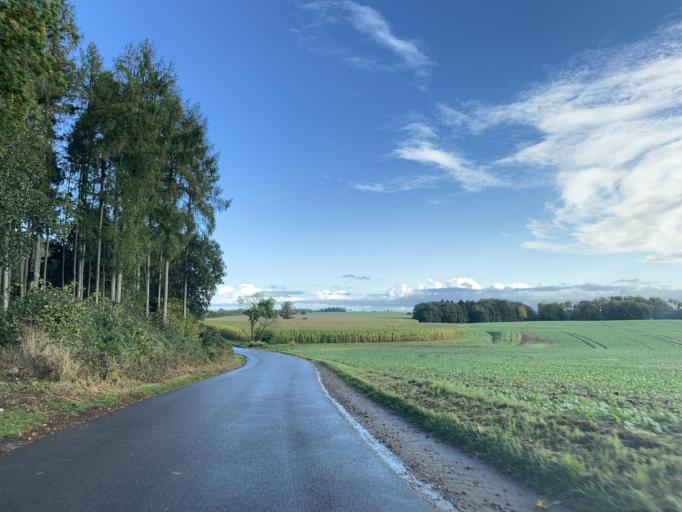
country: DE
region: Mecklenburg-Vorpommern
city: Blankensee
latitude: 53.4372
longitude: 13.2651
